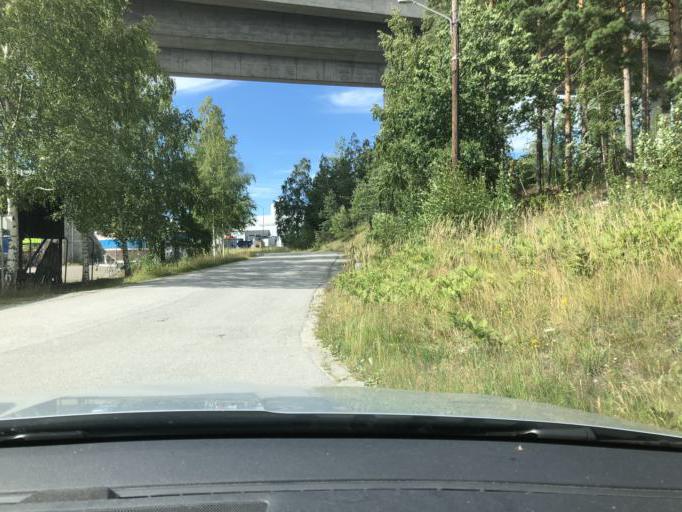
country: SE
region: Stockholm
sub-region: Sodertalje Kommun
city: Pershagen
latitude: 59.1635
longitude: 17.6517
